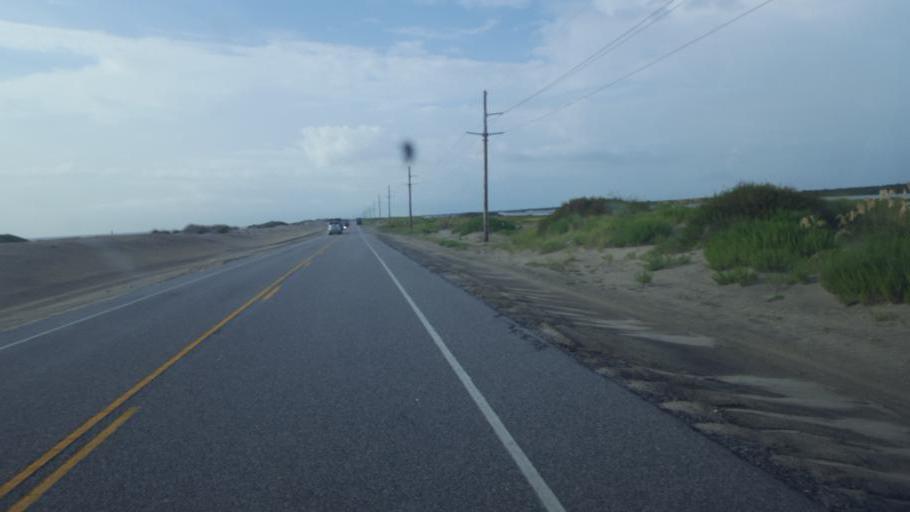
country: US
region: North Carolina
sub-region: Dare County
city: Wanchese
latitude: 35.7371
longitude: -75.5023
